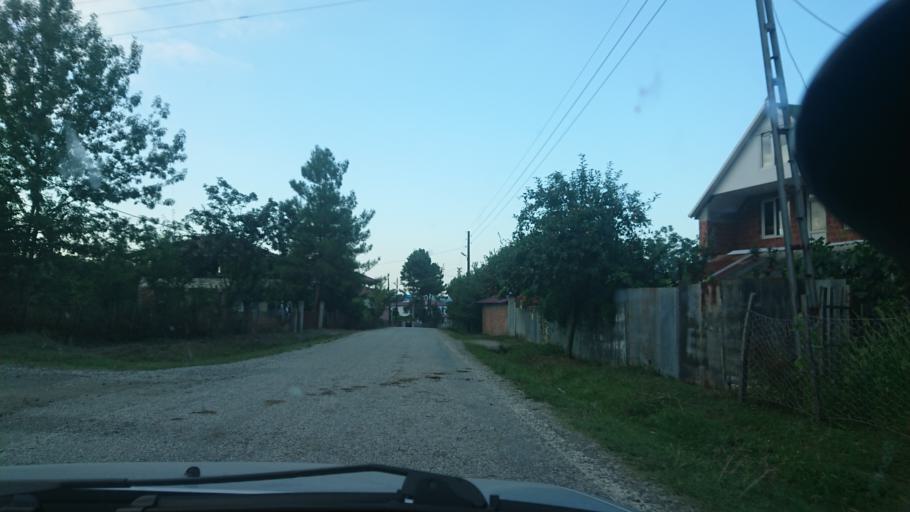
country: TR
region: Samsun
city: Dikbiyik
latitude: 41.1749
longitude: 36.5422
